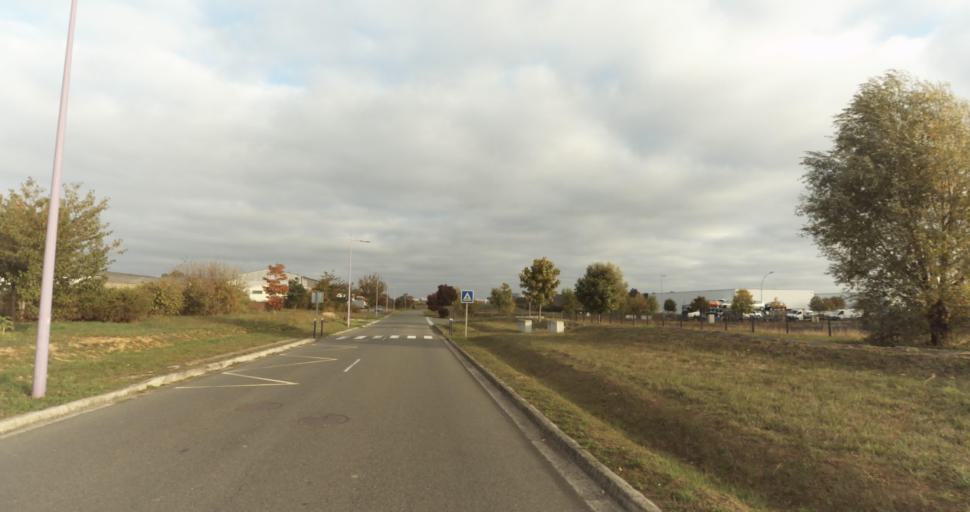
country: FR
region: Centre
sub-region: Departement d'Eure-et-Loir
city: Vernouillet
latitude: 48.7136
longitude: 1.3750
